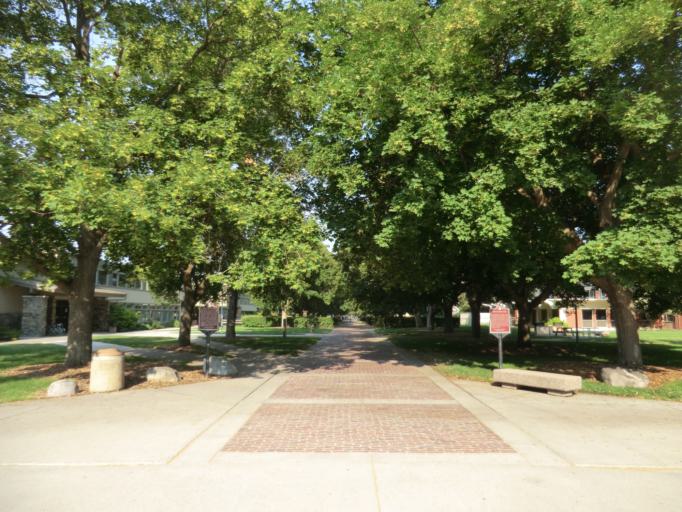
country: US
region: Montana
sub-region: Missoula County
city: Missoula
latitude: 46.8601
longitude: -113.9869
